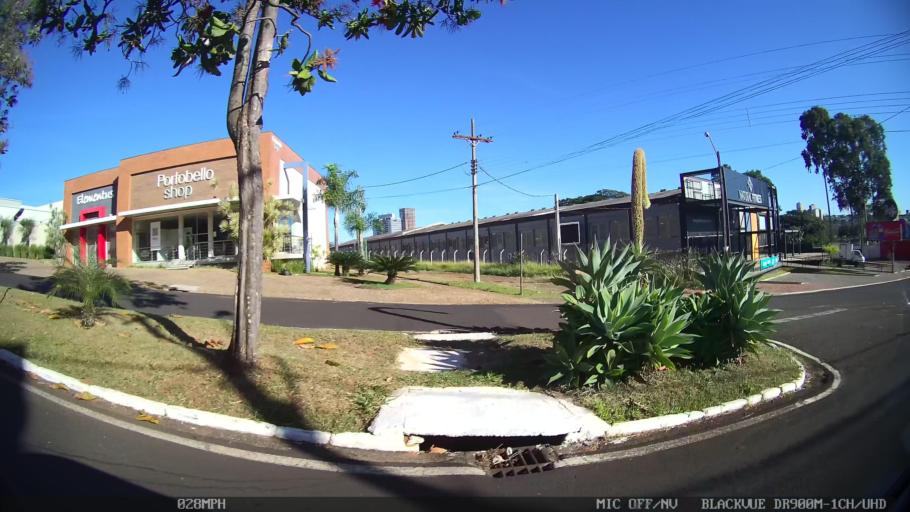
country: BR
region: Sao Paulo
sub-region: Franca
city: Franca
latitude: -20.5539
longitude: -47.4071
